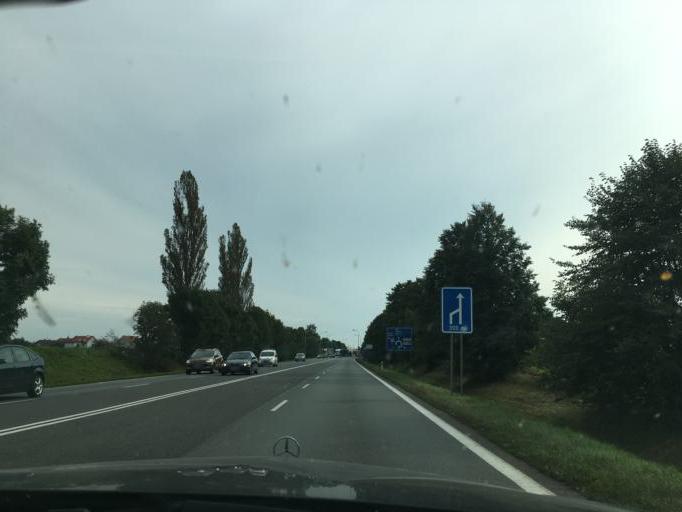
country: CZ
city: Predmerice nad Labem
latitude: 50.2250
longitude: 15.7895
